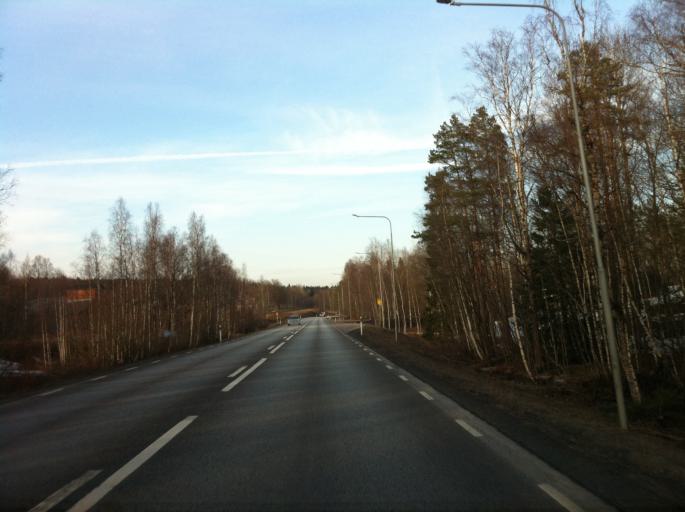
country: SE
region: Vaermland
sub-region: Filipstads Kommun
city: Filipstad
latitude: 59.7473
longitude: 14.2379
